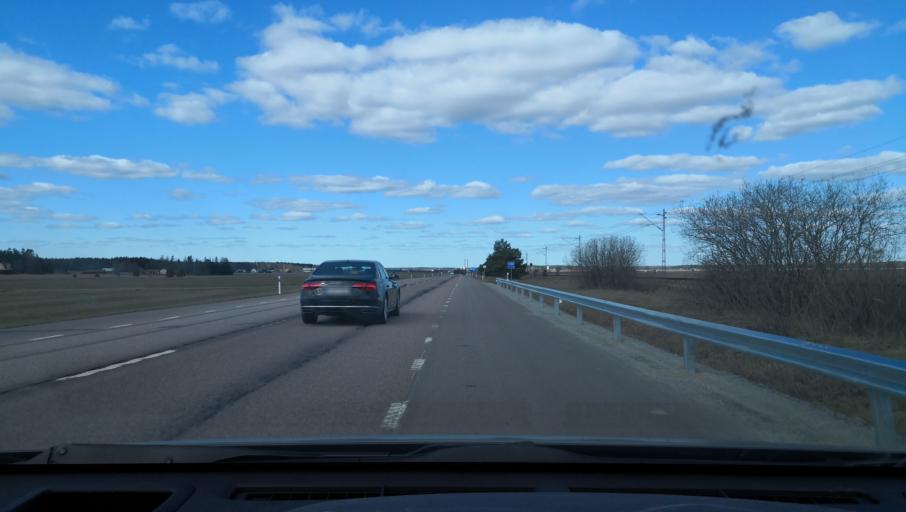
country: SE
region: Vaestmanland
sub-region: Sala Kommun
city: Sala
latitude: 59.8780
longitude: 16.6259
